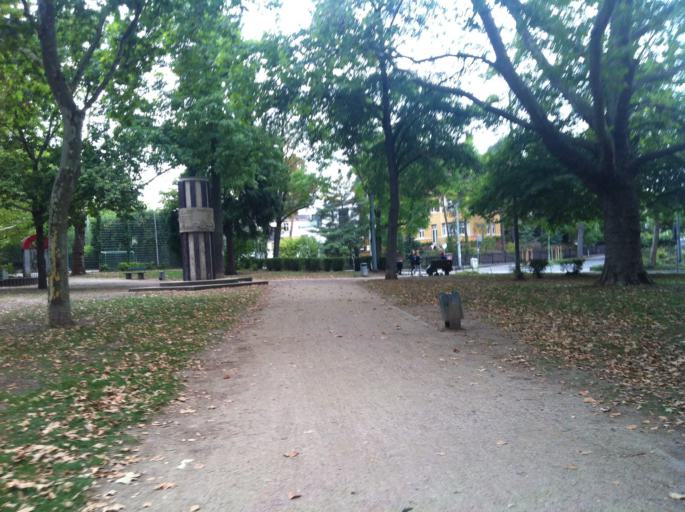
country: DE
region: Rheinland-Pfalz
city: Budenheim
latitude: 50.0014
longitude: 8.2065
